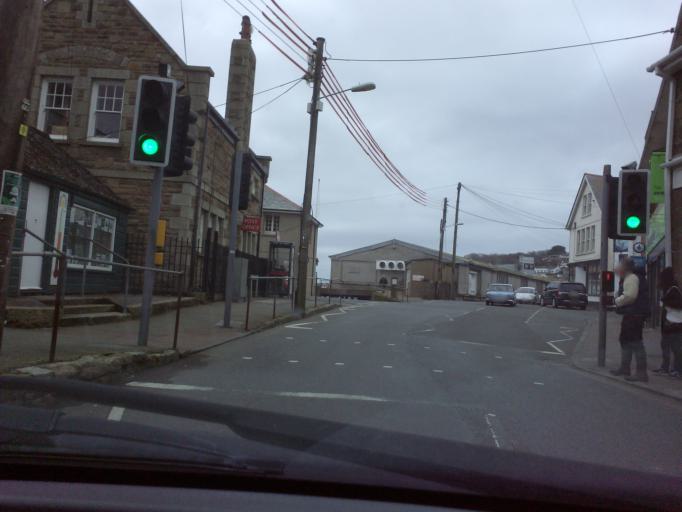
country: GB
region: England
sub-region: Cornwall
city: Penzance
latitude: 50.1063
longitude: -5.5496
